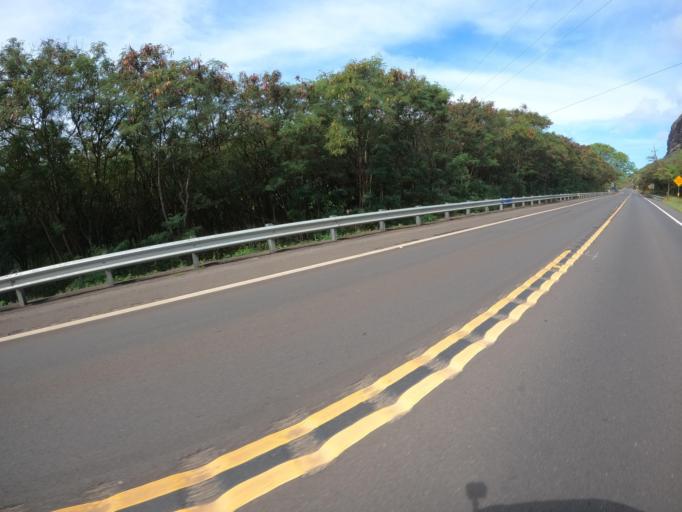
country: US
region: Hawaii
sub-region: Honolulu County
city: Makaha Valley
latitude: 21.5372
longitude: -158.2294
